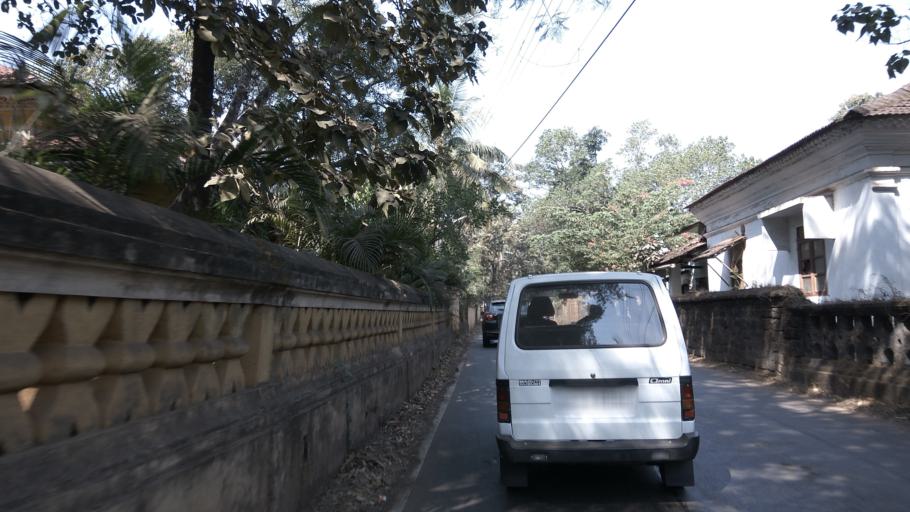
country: IN
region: Goa
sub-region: North Goa
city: Vagator
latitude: 15.5947
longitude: 73.7533
